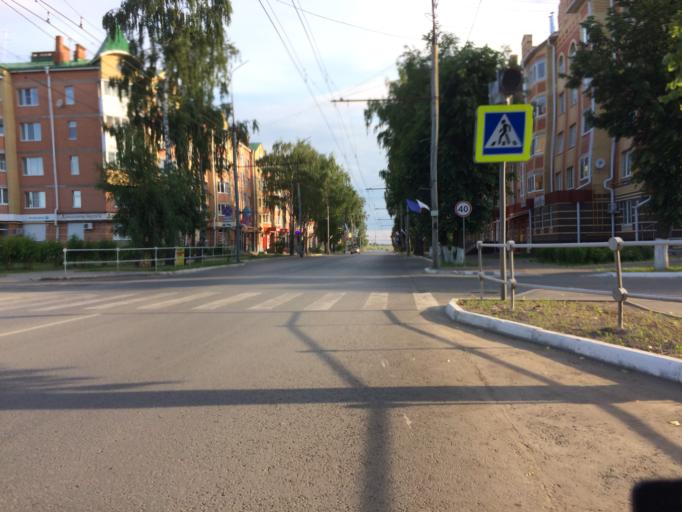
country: RU
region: Mariy-El
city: Medvedevo
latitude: 56.6361
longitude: 47.8032
